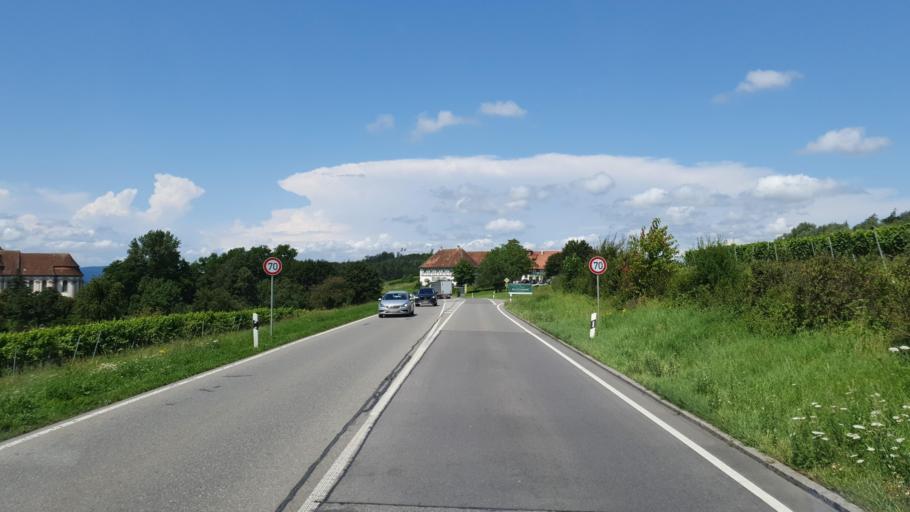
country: DE
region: Baden-Wuerttemberg
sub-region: Tuebingen Region
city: Uhldingen-Muhlhofen
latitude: 47.7458
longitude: 9.2234
